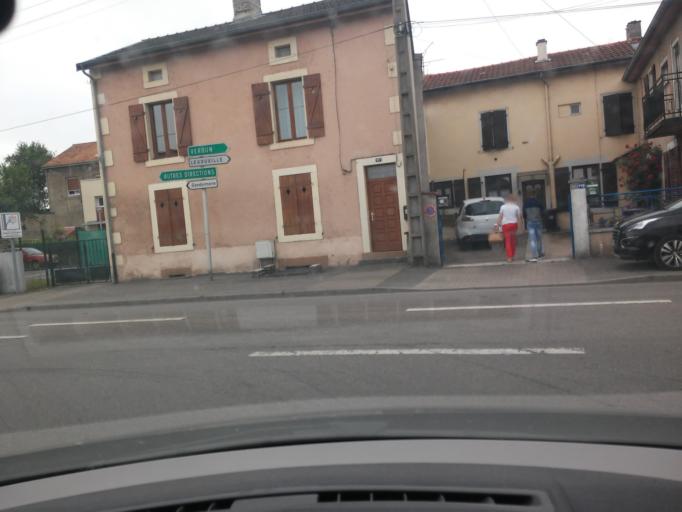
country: FR
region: Lorraine
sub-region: Departement de la Meuse
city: Commercy
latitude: 48.7677
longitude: 5.5802
